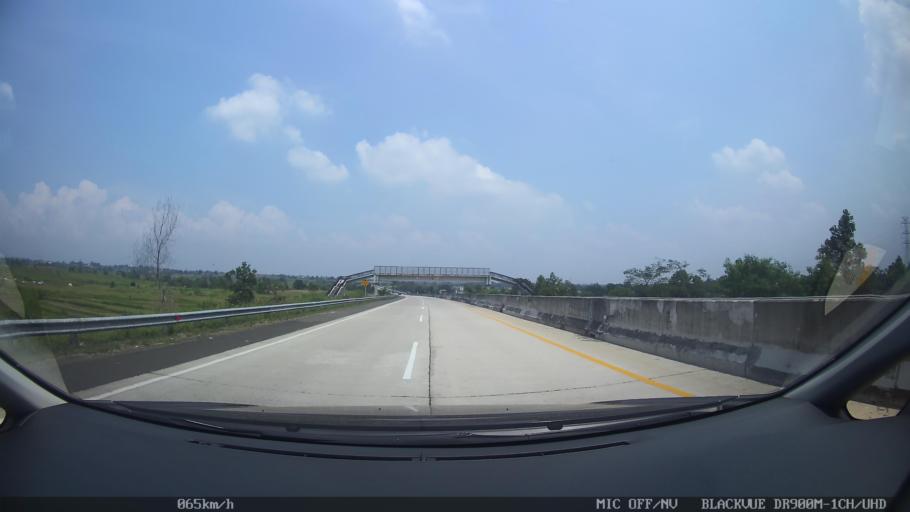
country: ID
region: Lampung
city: Kedaton
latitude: -5.3450
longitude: 105.3173
